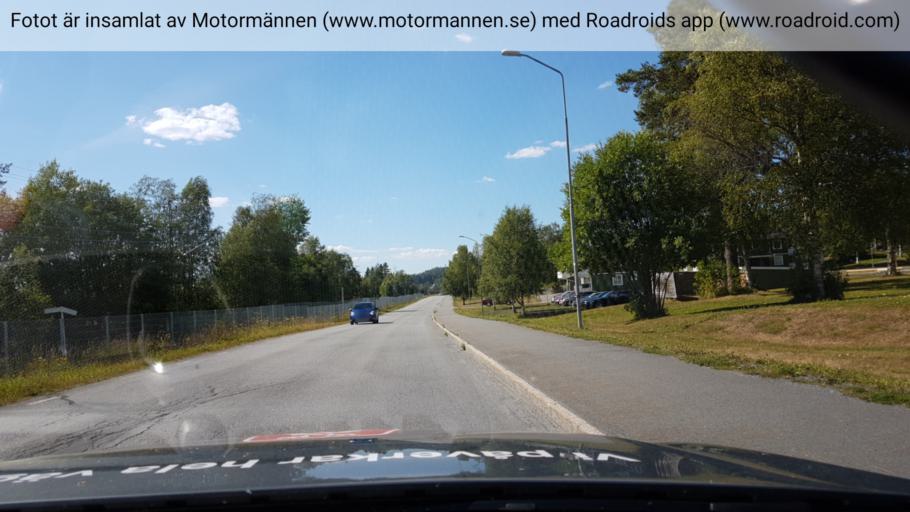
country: SE
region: Jaemtland
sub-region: Are Kommun
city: Jarpen
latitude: 63.3063
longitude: 13.6739
